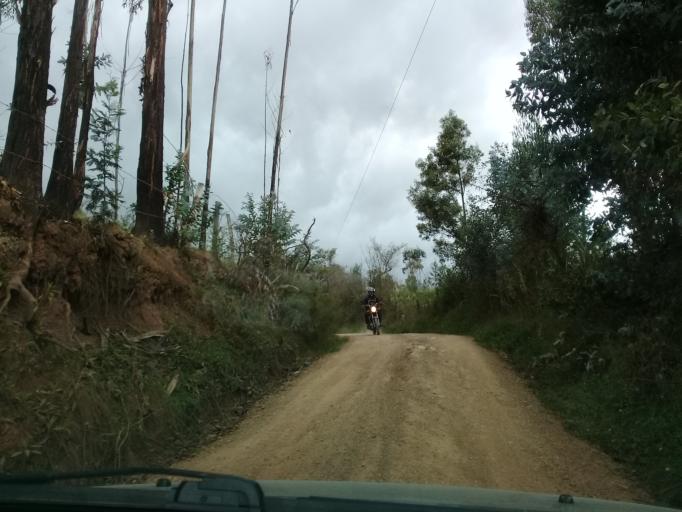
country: CO
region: Cundinamarca
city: Cucunuba
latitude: 5.2829
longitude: -73.7466
